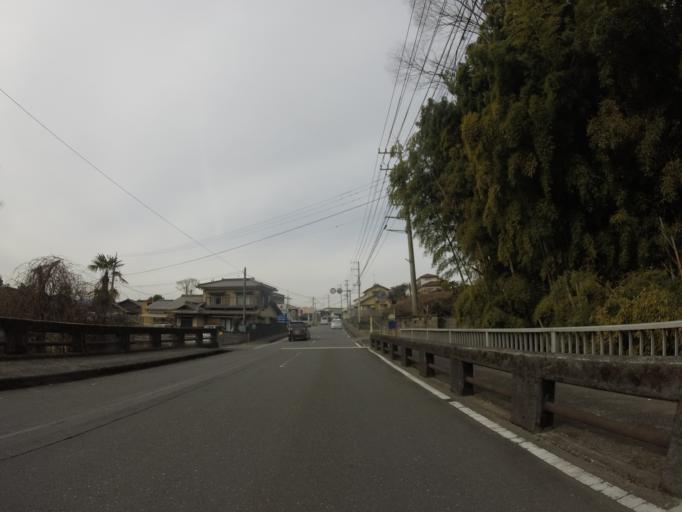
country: JP
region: Shizuoka
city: Fujinomiya
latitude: 35.2182
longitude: 138.6564
